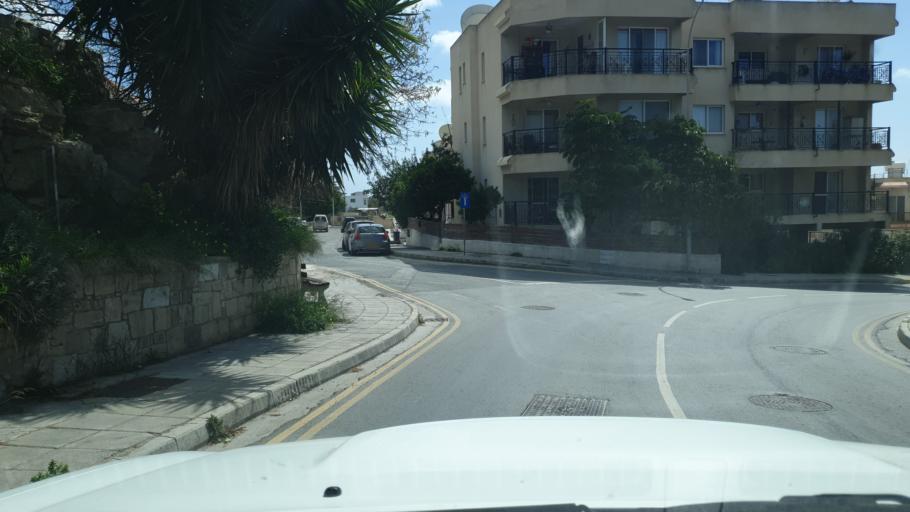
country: CY
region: Pafos
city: Paphos
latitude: 34.7570
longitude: 32.4572
